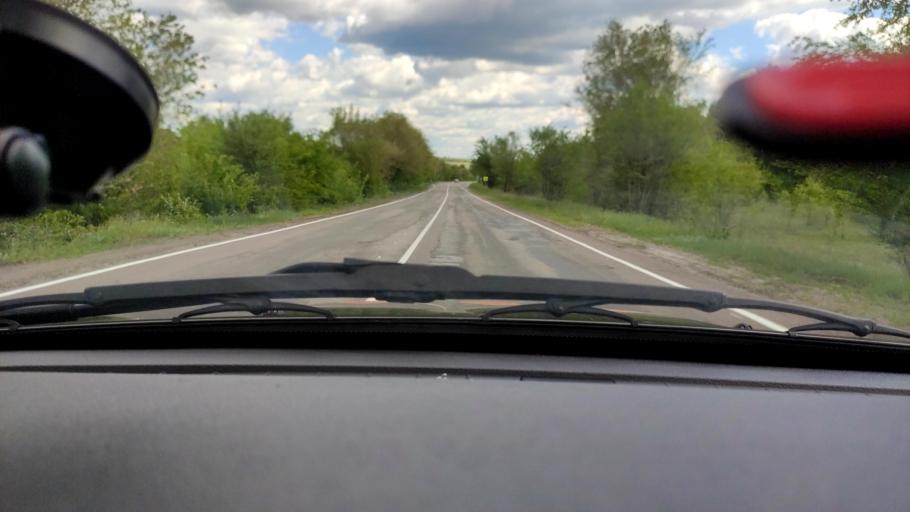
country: RU
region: Belgorod
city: Krasnoye
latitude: 51.0680
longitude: 38.8047
